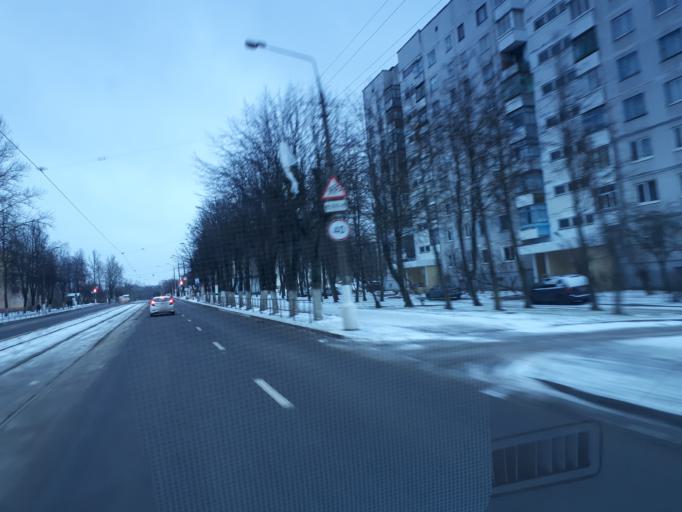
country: BY
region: Vitebsk
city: Vitebsk
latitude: 55.1710
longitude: 30.1399
